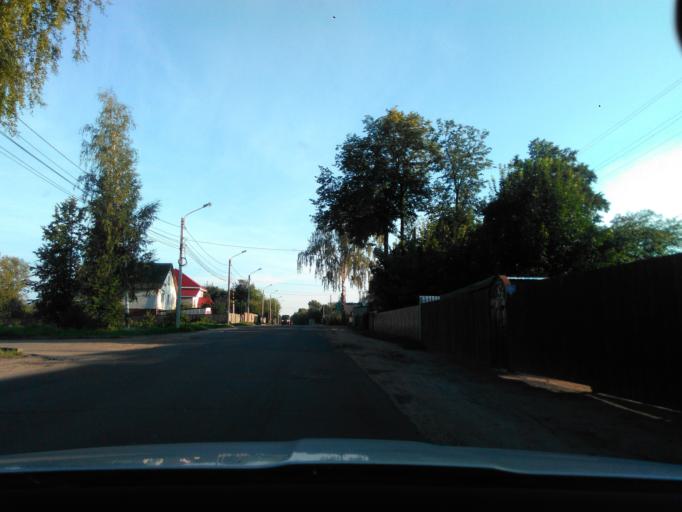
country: RU
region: Tverskaya
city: Konakovo
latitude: 56.6991
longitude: 36.7670
